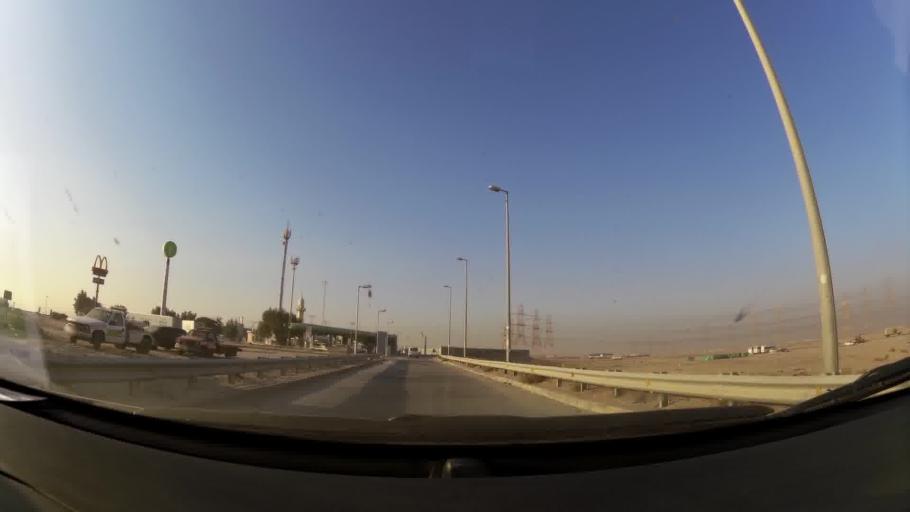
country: KW
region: Al Ahmadi
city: Al Fahahil
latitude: 28.7985
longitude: 48.2705
